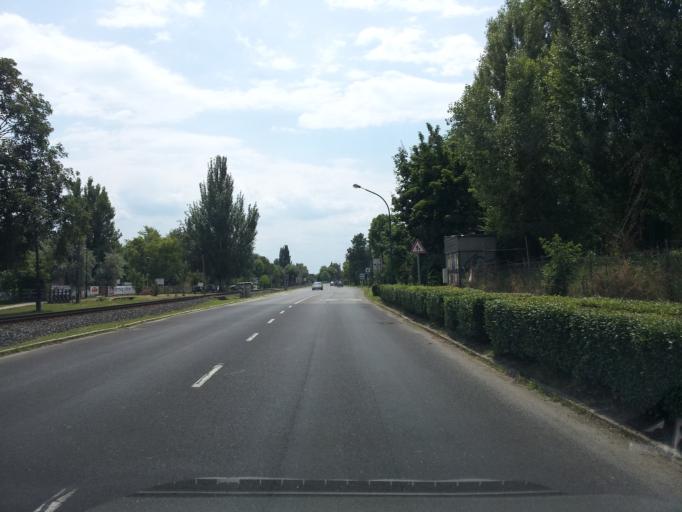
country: HU
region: Veszprem
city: Balatonalmadi
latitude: 47.0219
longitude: 18.0081
